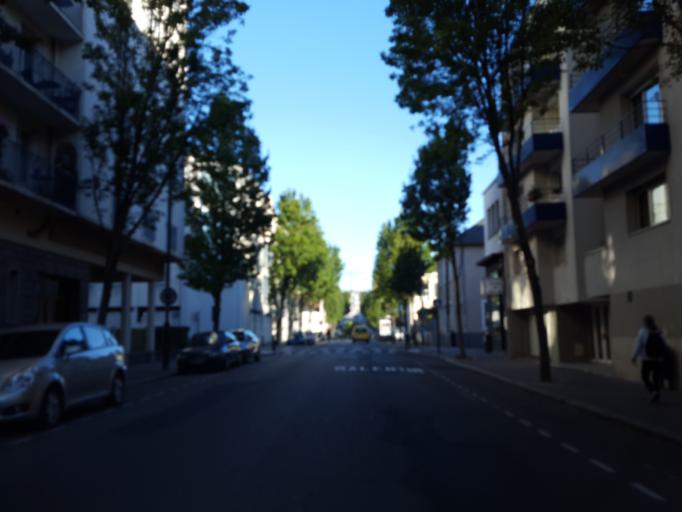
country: FR
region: Pays de la Loire
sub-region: Departement de la Loire-Atlantique
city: Nantes
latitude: 47.2115
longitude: -1.5712
